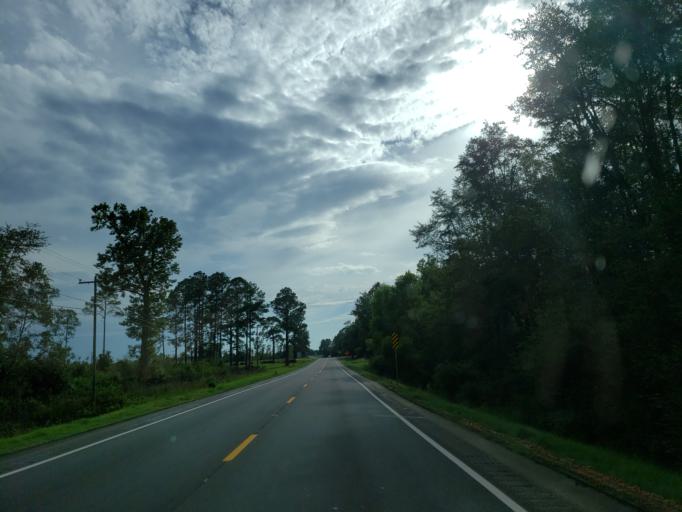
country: US
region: Georgia
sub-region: Irwin County
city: Ocilla
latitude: 31.5607
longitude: -83.3581
